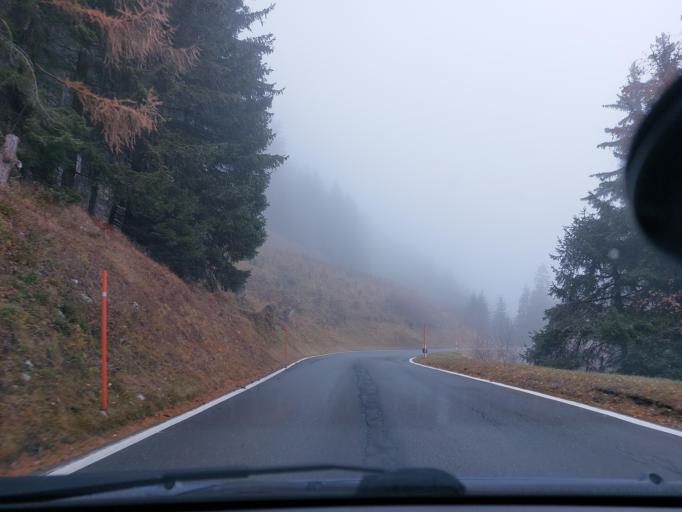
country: CH
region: Valais
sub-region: Conthey District
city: Basse-Nendaz
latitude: 46.1613
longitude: 7.3125
